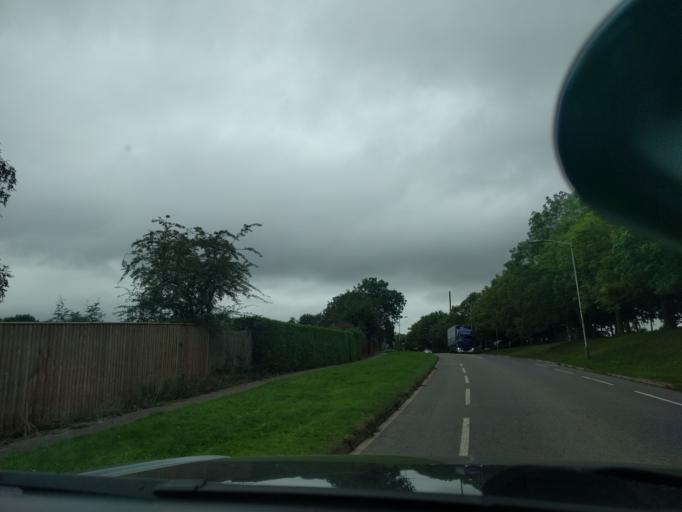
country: GB
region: England
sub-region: Wiltshire
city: Corsham
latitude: 51.4295
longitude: -2.1948
